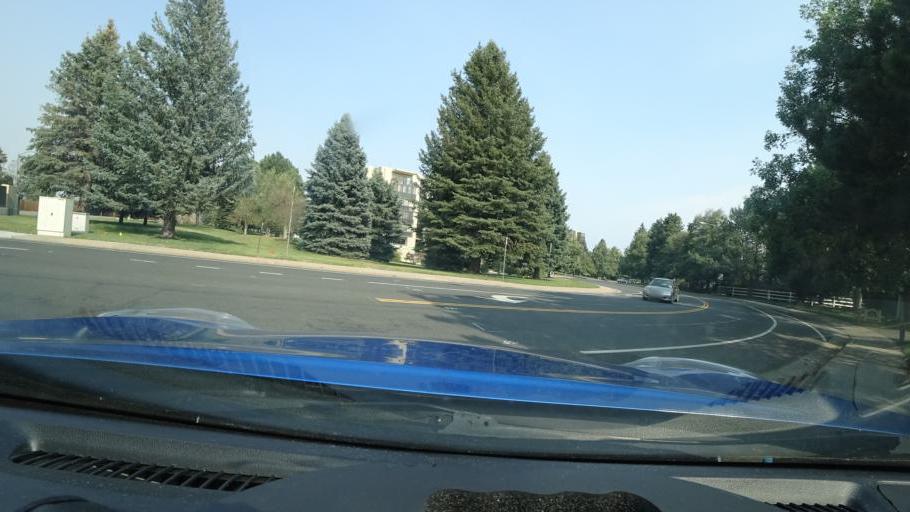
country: US
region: Colorado
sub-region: Adams County
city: Aurora
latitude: 39.6673
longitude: -104.8217
